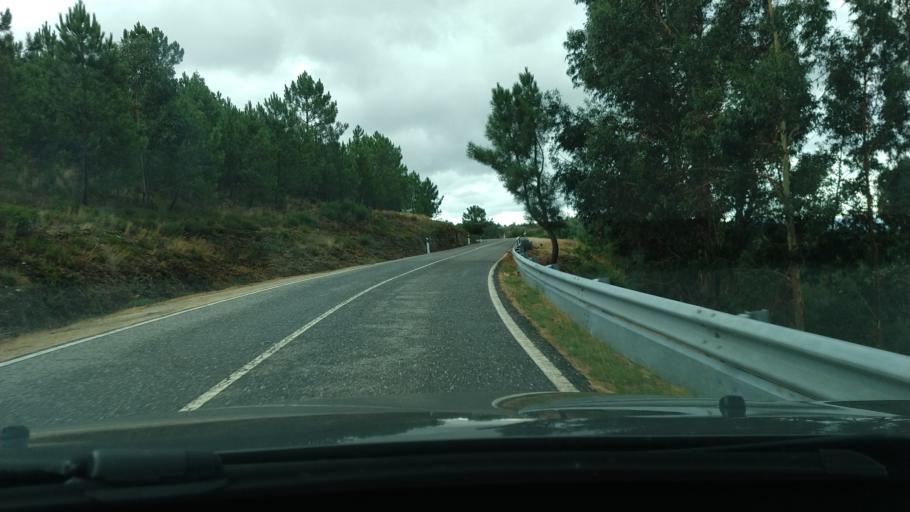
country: PT
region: Castelo Branco
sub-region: Covilha
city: Covilha
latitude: 40.2369
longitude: -7.6757
